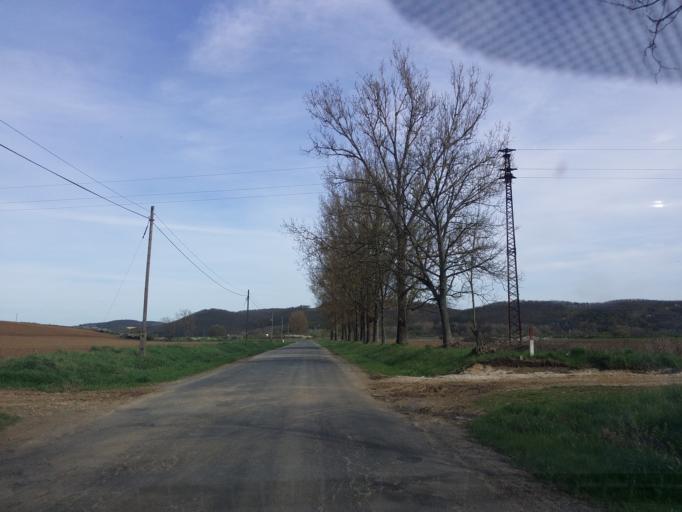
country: HU
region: Borsod-Abauj-Zemplen
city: Szendro
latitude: 48.4499
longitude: 20.7482
